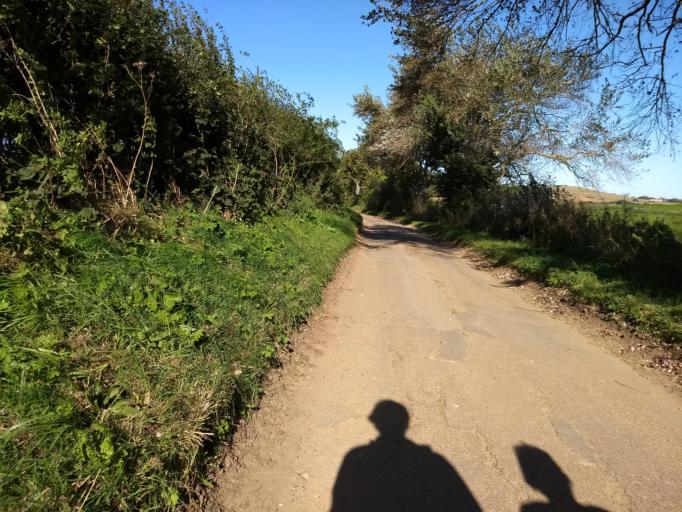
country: GB
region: England
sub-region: Isle of Wight
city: Chale
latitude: 50.6411
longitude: -1.2999
